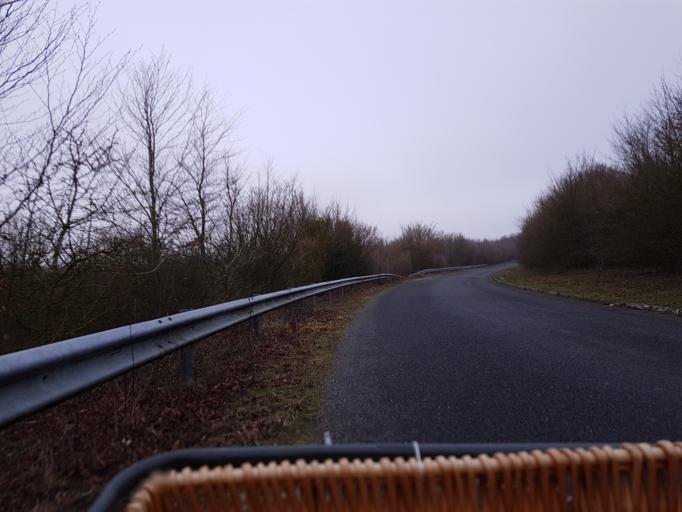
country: GB
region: England
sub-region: Cambridgeshire
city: Duxford
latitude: 52.0759
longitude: 0.1956
